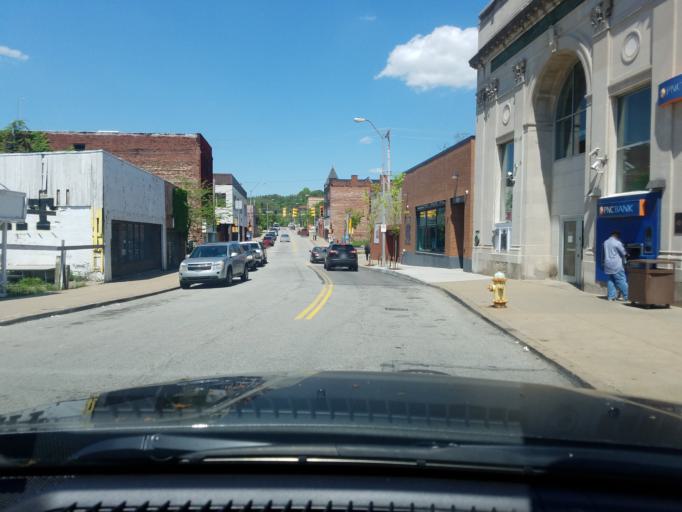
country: US
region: Pennsylvania
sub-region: Allegheny County
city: Wilkinsburg
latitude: 40.4550
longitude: -79.8972
